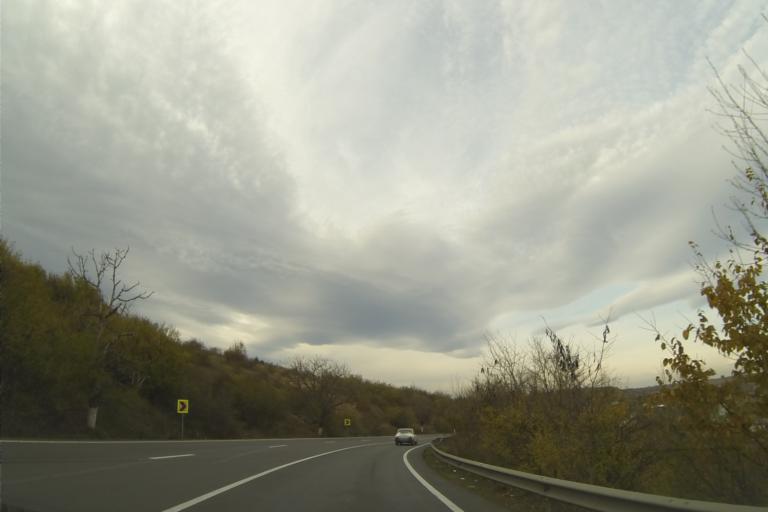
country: RO
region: Olt
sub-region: Comuna Scornicesti
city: Margineni Slobozia
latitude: 44.5382
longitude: 24.5384
